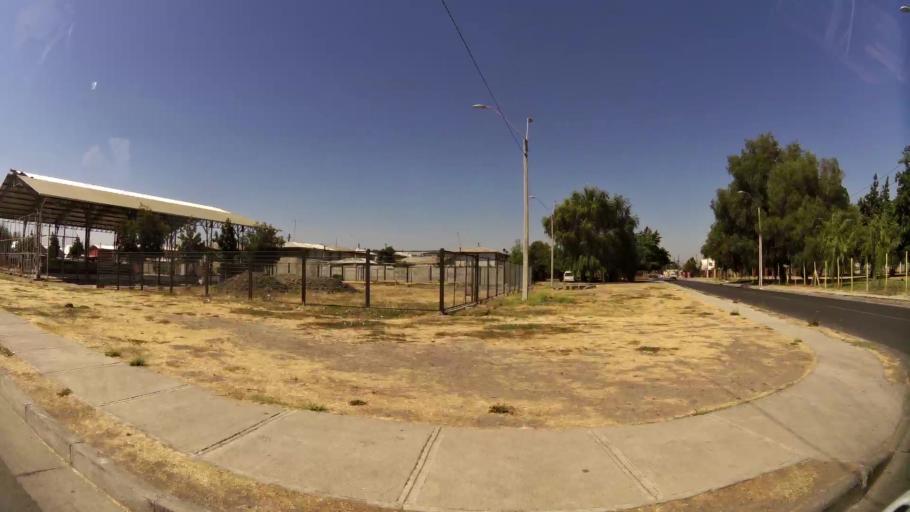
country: CL
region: Maule
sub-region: Provincia de Curico
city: Curico
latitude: -34.9639
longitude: -71.2400
